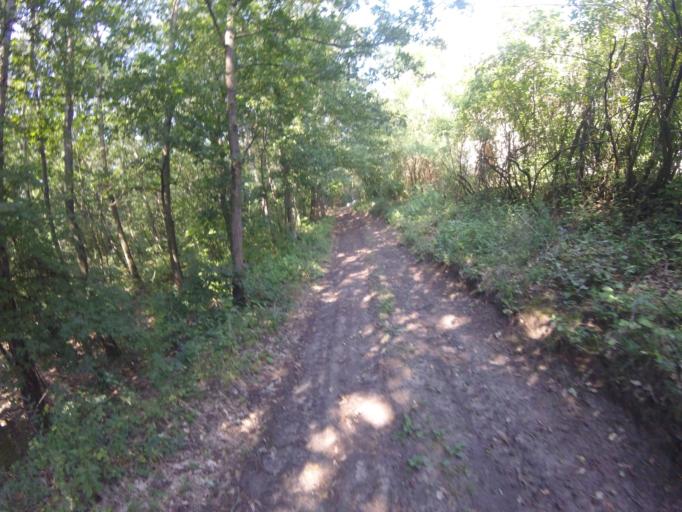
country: HU
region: Nograd
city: Bujak
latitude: 47.8865
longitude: 19.5345
